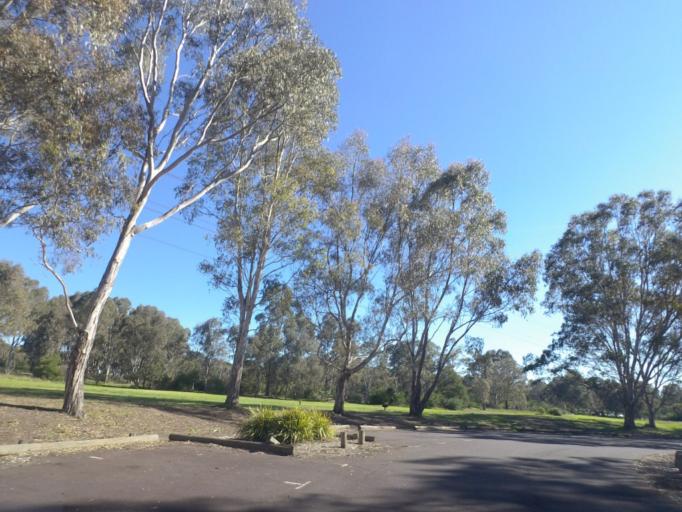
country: AU
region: Victoria
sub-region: Banyule
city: Viewbank
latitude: -37.7526
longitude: 145.0988
